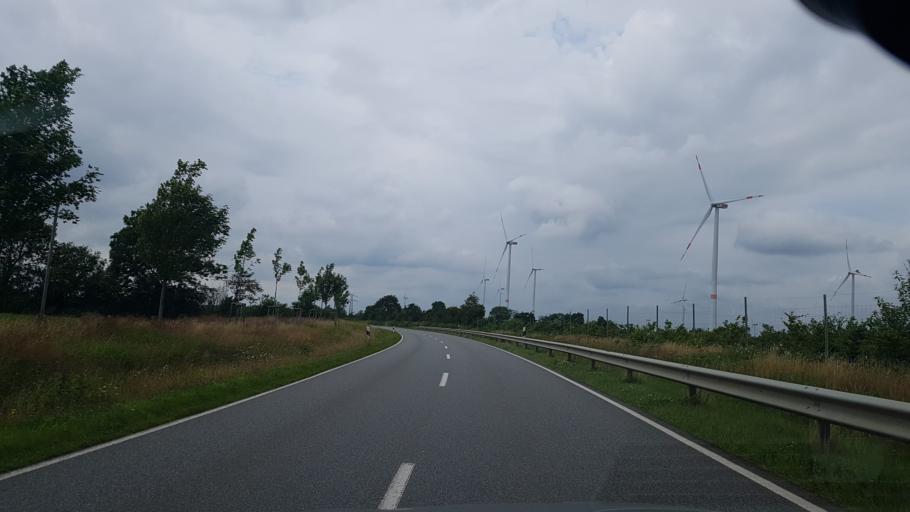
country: DE
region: Schleswig-Holstein
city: Jardelund
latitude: 54.8417
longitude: 9.2096
